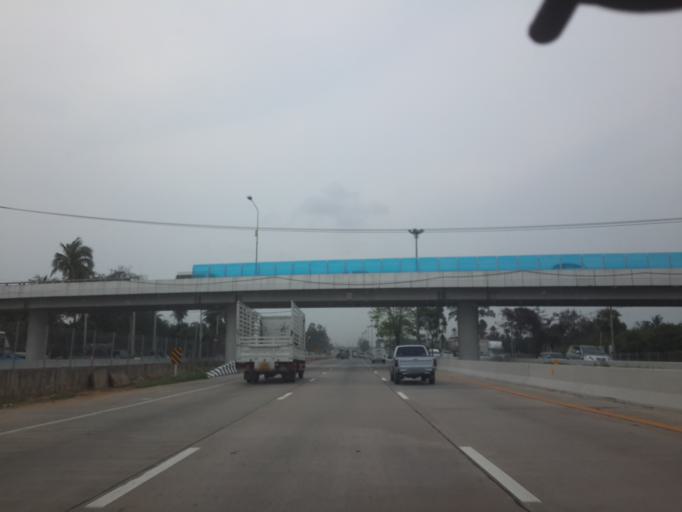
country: TH
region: Chon Buri
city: Ban Talat Bueng
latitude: 13.0511
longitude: 100.9961
